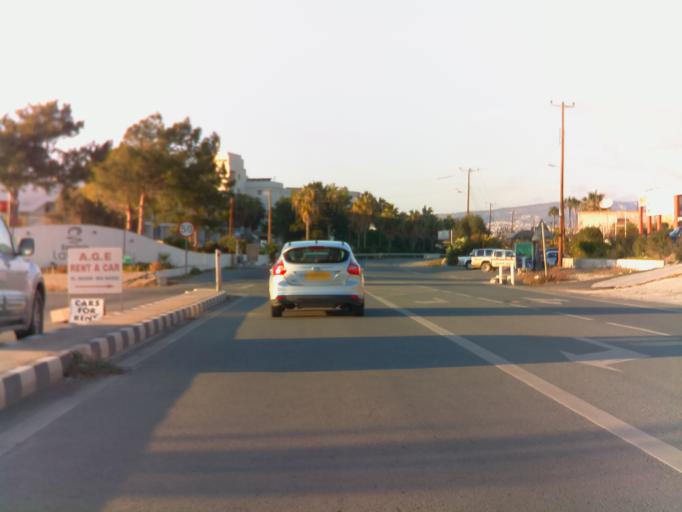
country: CY
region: Pafos
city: Chlorakas
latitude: 34.8047
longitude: 32.3974
